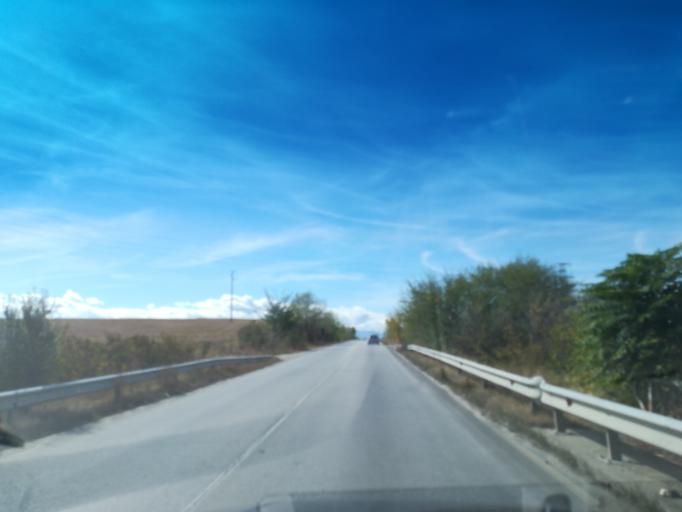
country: BG
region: Plovdiv
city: Stamboliyski
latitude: 42.1312
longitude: 24.6061
